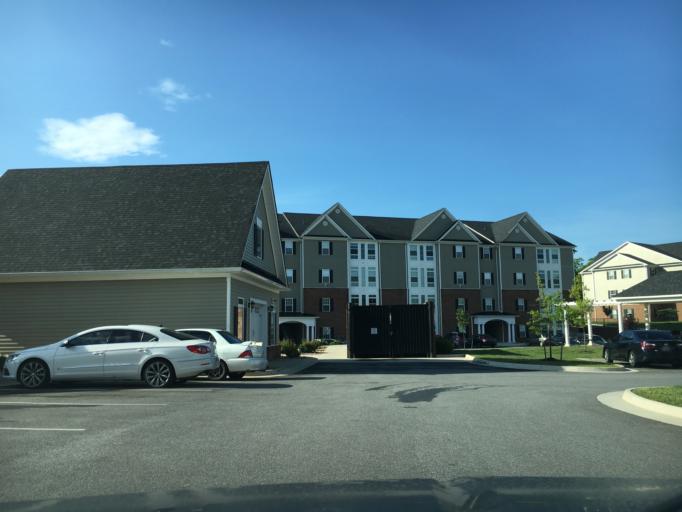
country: US
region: Virginia
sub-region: Bedford County
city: Forest
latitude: 37.3700
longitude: -79.2568
